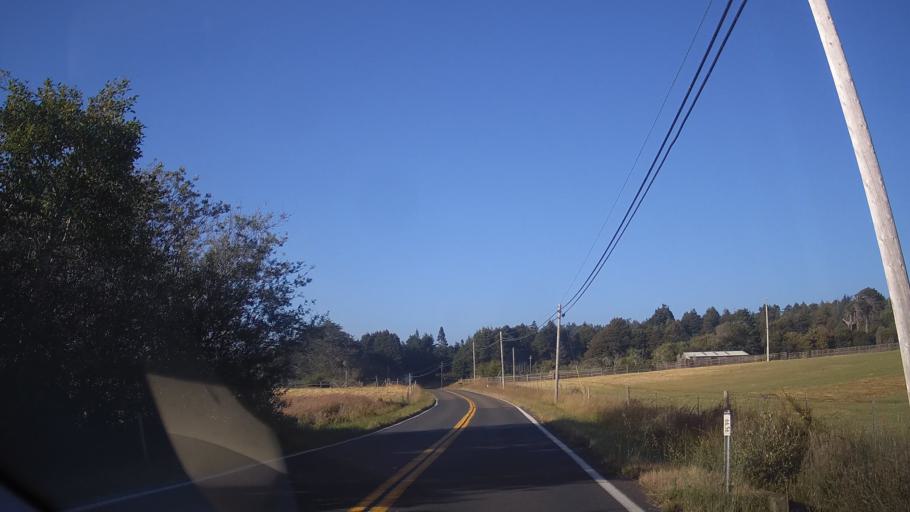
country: US
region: California
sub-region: Mendocino County
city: Fort Bragg
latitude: 39.5050
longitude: -123.7688
